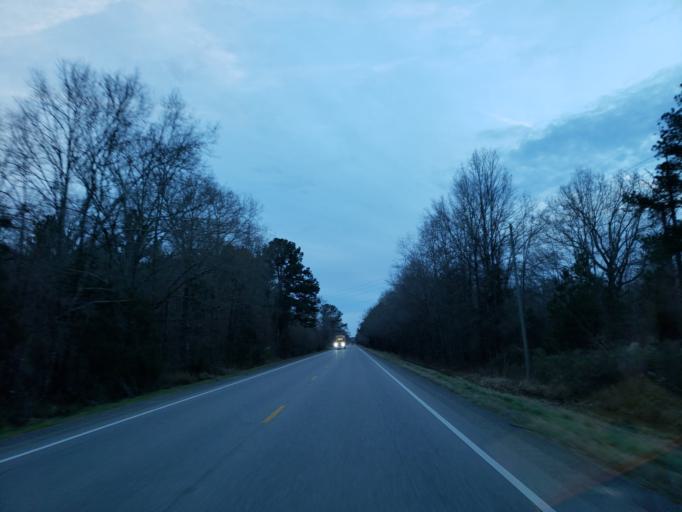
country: US
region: Alabama
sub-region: Sumter County
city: Livingston
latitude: 32.8227
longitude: -88.3103
